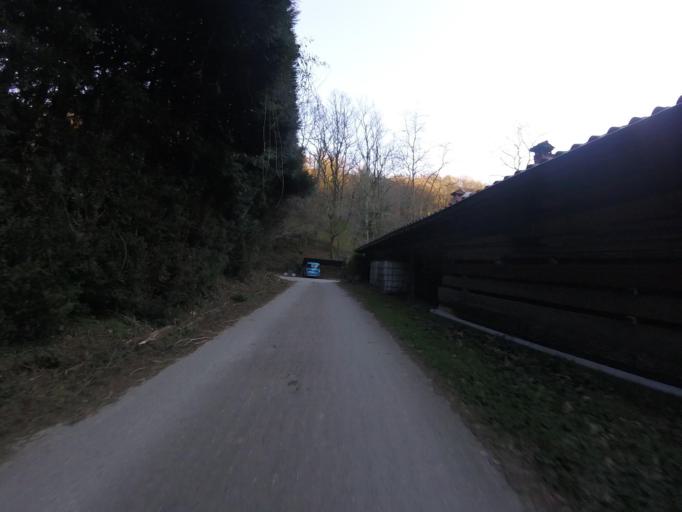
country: ES
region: Basque Country
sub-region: Provincia de Guipuzcoa
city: Errenteria
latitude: 43.2648
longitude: -1.8564
